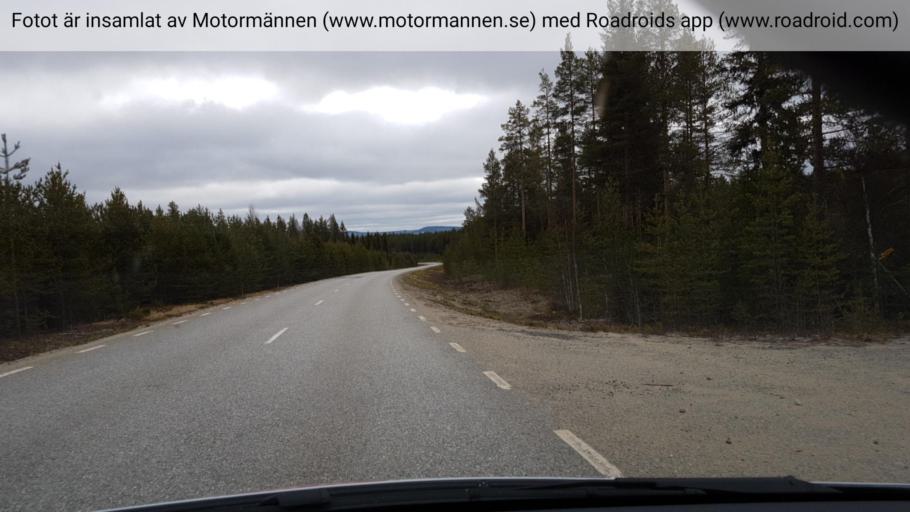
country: SE
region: Vaesterbotten
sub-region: Lycksele Kommun
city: Lycksele
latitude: 64.0236
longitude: 18.4491
